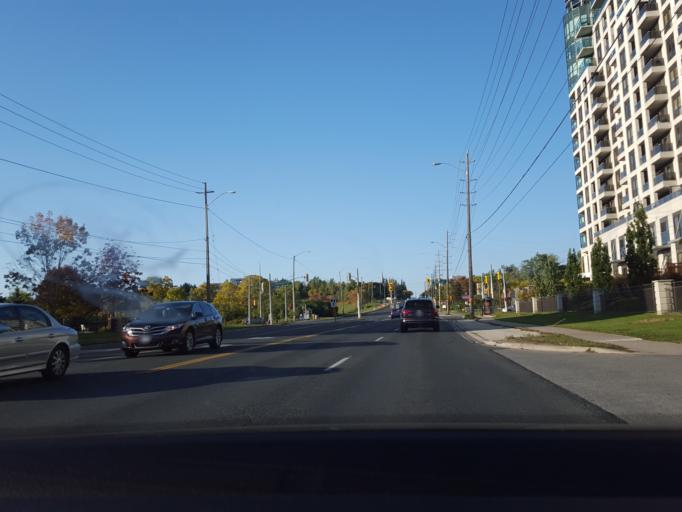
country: CA
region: Ontario
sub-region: York
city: Richmond Hill
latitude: 43.8656
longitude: -79.4359
